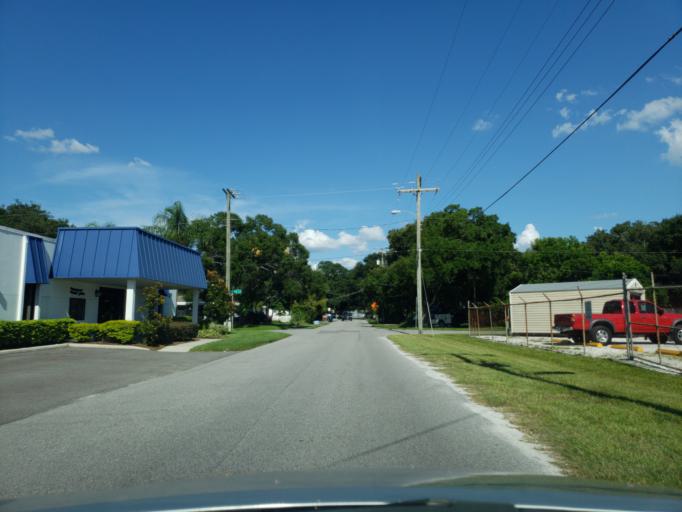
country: US
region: Florida
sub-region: Hillsborough County
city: Tampa
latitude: 27.9604
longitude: -82.5036
